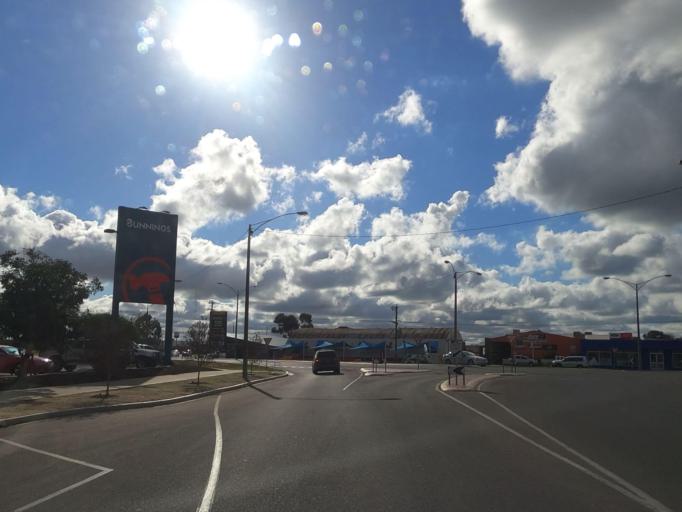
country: AU
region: Victoria
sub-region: Swan Hill
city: Swan Hill
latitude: -35.3344
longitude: 143.5568
